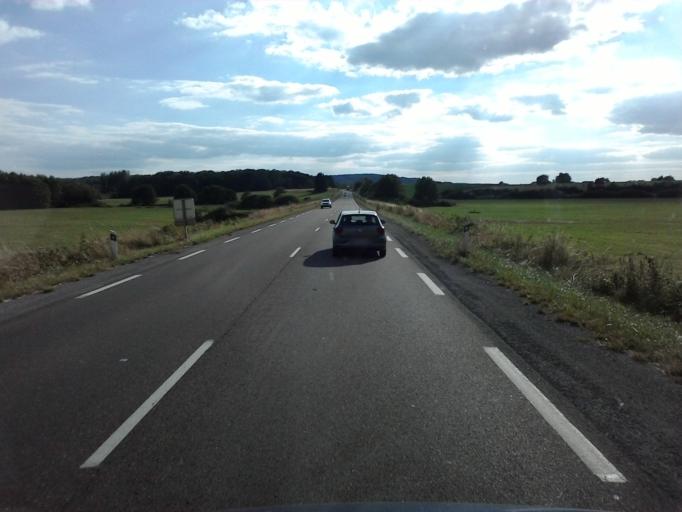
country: FR
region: Franche-Comte
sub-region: Departement de la Haute-Saone
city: Saint-Sauveur
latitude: 47.7721
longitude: 6.3551
